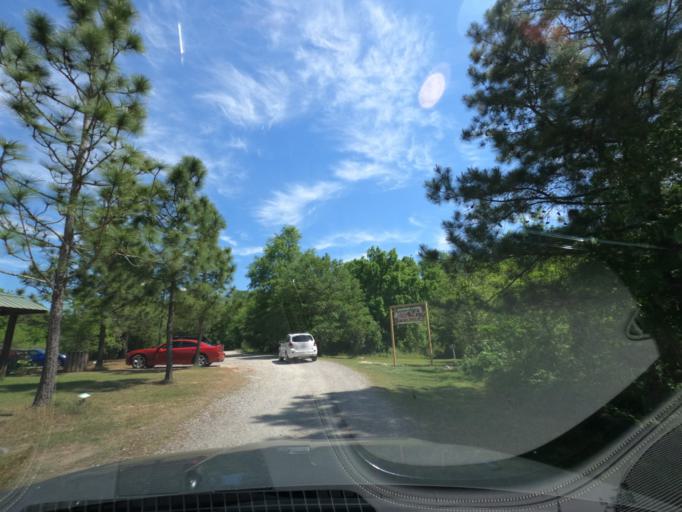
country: US
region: Georgia
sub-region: Richmond County
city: Augusta
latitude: 33.3847
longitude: -81.9673
